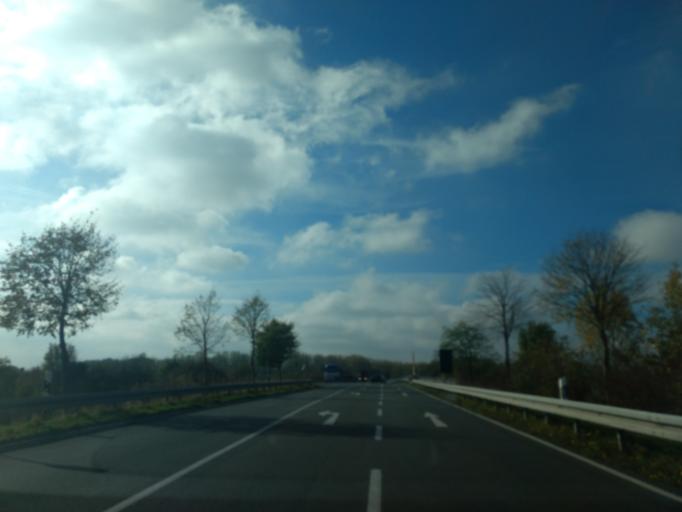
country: DE
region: Lower Saxony
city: Bad Rothenfelde
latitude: 52.1192
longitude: 8.1810
